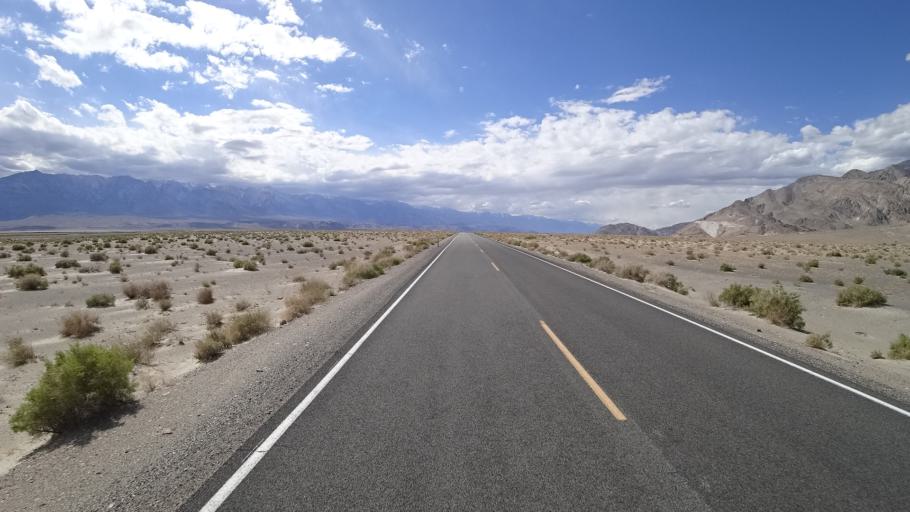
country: US
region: California
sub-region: Inyo County
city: Lone Pine
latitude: 36.5477
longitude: -117.9447
